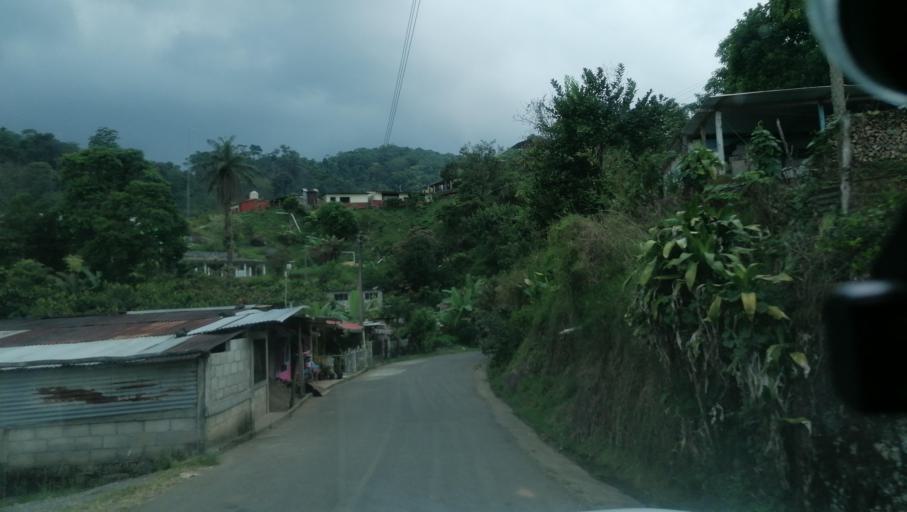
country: MX
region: Chiapas
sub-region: Cacahoatan
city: Benito Juarez
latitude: 15.0743
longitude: -92.1706
